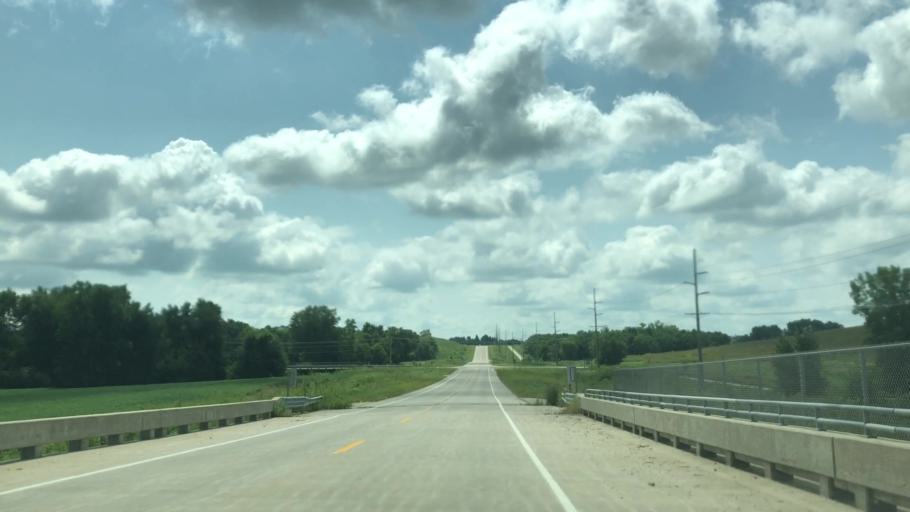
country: US
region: Iowa
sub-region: Marshall County
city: Marshalltown
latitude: 42.0203
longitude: -92.9601
